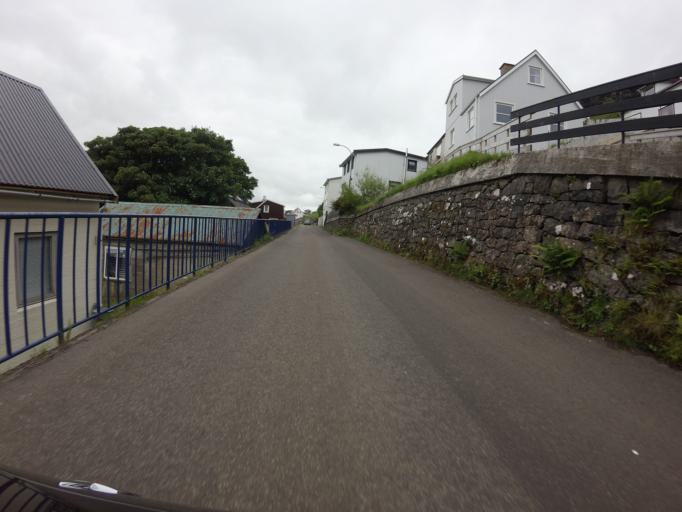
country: FO
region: Eysturoy
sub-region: Eidi
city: Eidi
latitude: 62.2735
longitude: -7.0922
